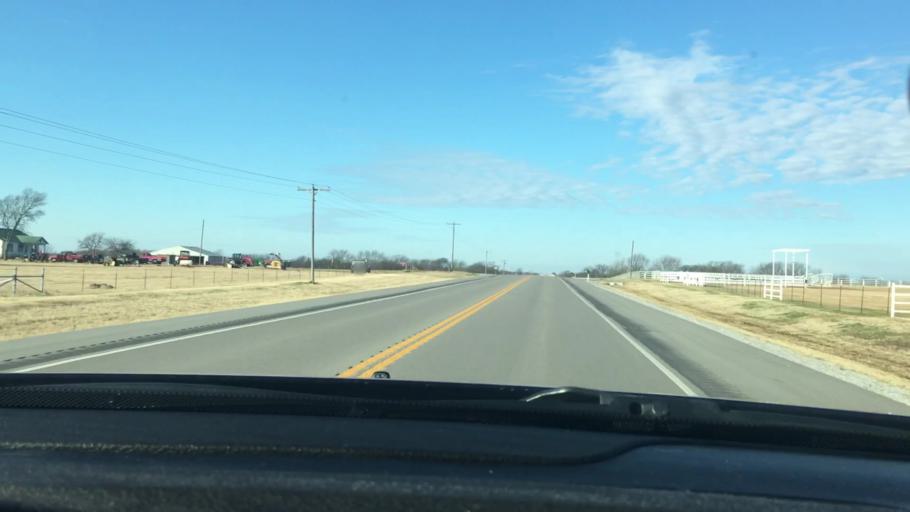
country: US
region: Oklahoma
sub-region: Love County
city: Marietta
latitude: 33.9404
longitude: -97.1919
